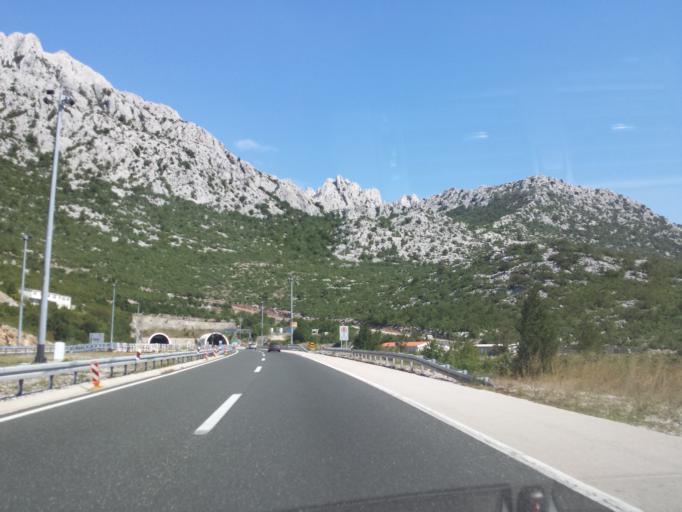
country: HR
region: Zadarska
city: Obrovac
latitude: 44.2540
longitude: 15.6469
